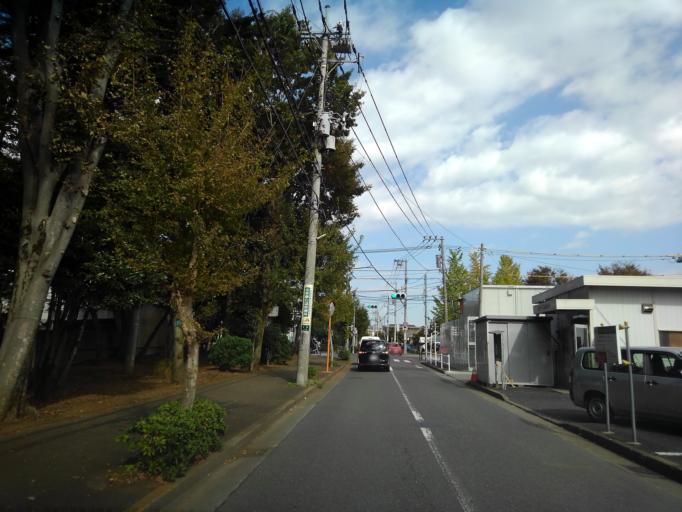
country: JP
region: Tokyo
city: Higashimurayama-shi
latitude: 35.7545
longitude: 139.4690
